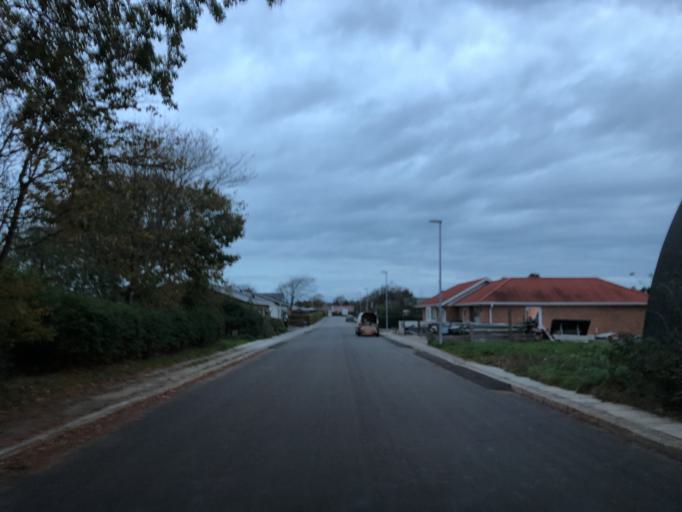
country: DK
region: Central Jutland
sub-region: Holstebro Kommune
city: Ulfborg
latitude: 56.3438
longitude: 8.3395
